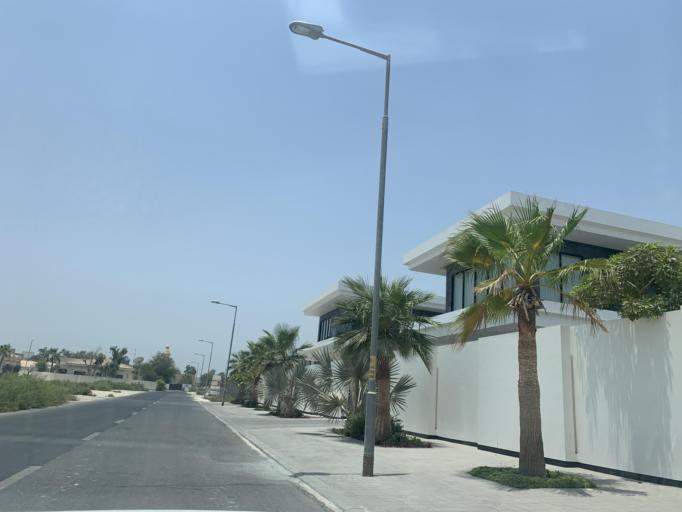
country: BH
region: Manama
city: Jidd Hafs
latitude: 26.2110
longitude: 50.4786
